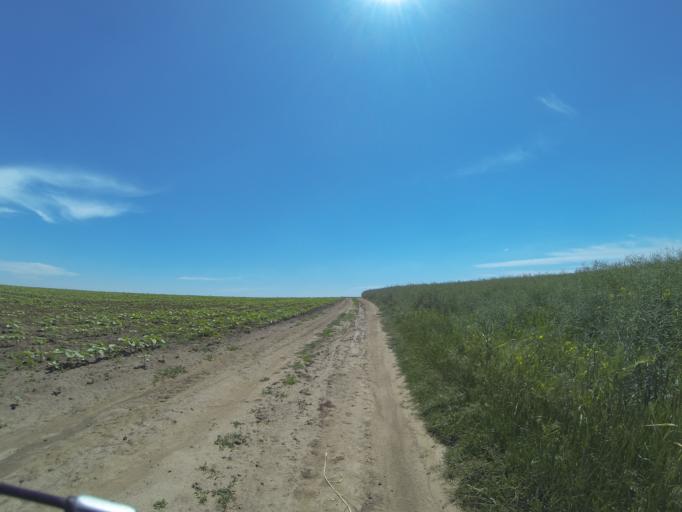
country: RO
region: Dolj
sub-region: Comuna Leu
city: Zanoaga
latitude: 44.2005
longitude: 24.0640
